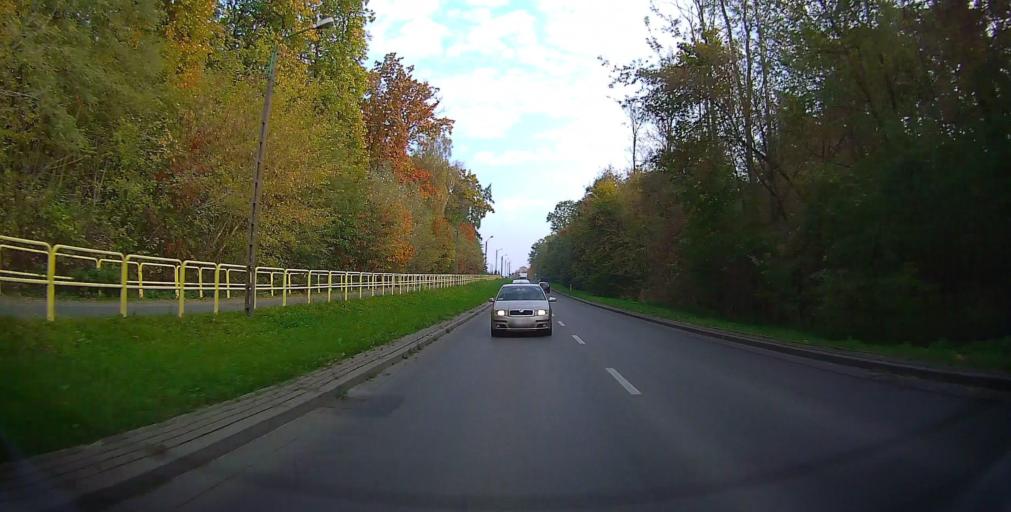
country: PL
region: Masovian Voivodeship
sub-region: Powiat grojecki
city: Mogielnica
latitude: 51.6986
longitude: 20.7293
